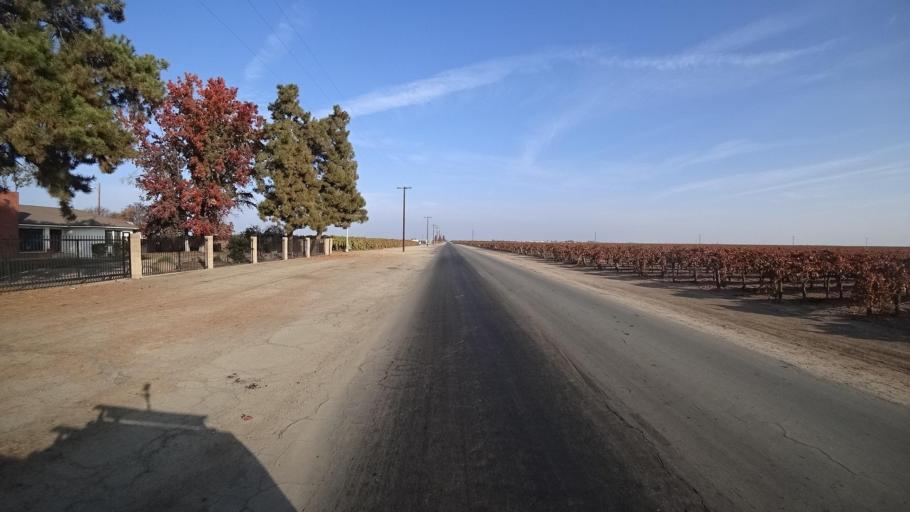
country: US
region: California
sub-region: Kern County
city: Delano
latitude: 35.7483
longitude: -119.1870
